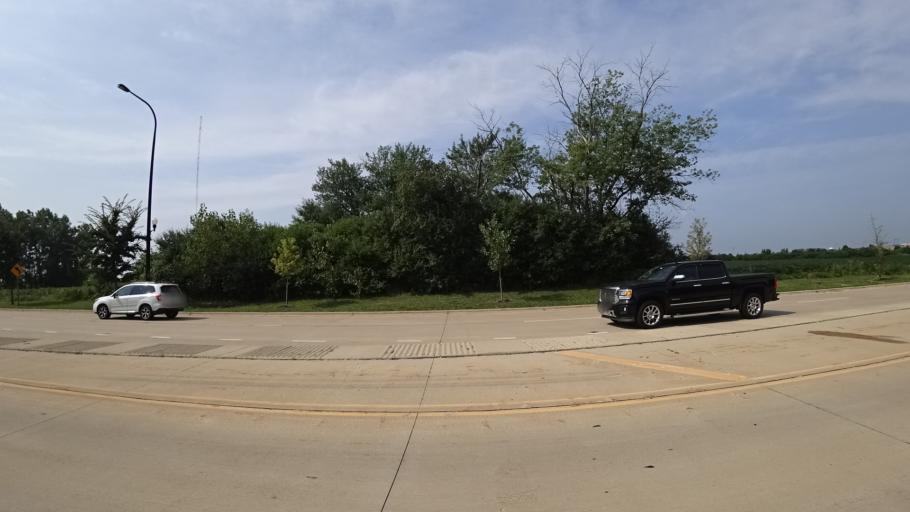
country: US
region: Illinois
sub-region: Cook County
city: Orland Hills
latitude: 41.5590
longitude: -87.8475
